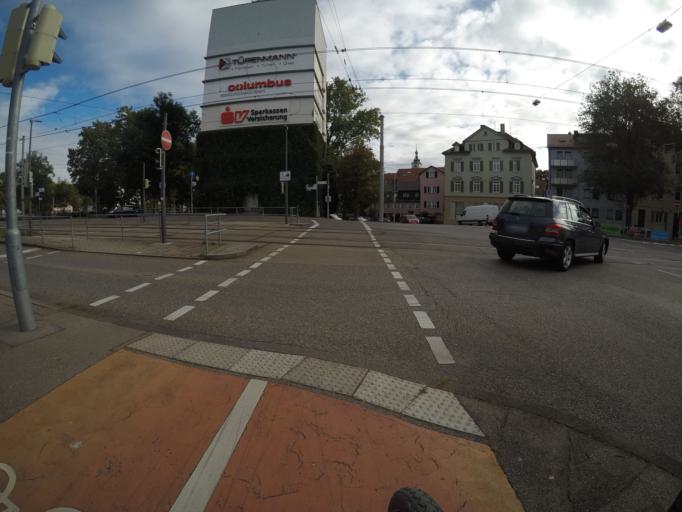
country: DE
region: Baden-Wuerttemberg
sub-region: Regierungsbezirk Stuttgart
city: Stuttgart-Ost
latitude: 48.8046
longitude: 9.2115
